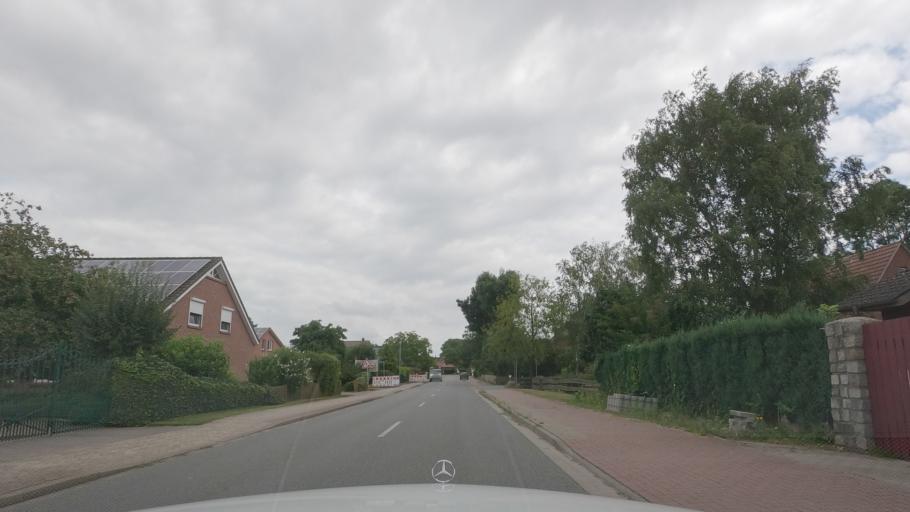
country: DE
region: Lower Saxony
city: Neuenkirchen
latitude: 53.2836
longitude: 8.5328
